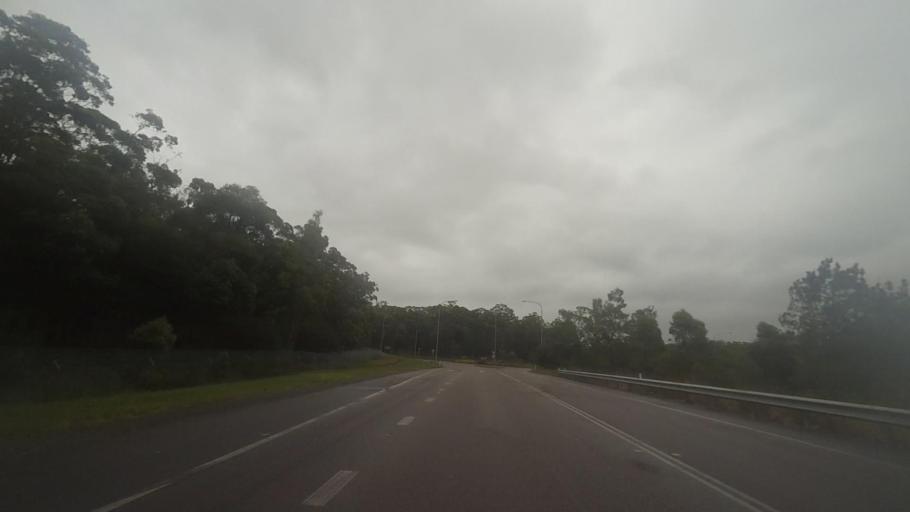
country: AU
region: New South Wales
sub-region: Port Stephens Shire
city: Medowie
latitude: -32.6480
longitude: 151.9165
